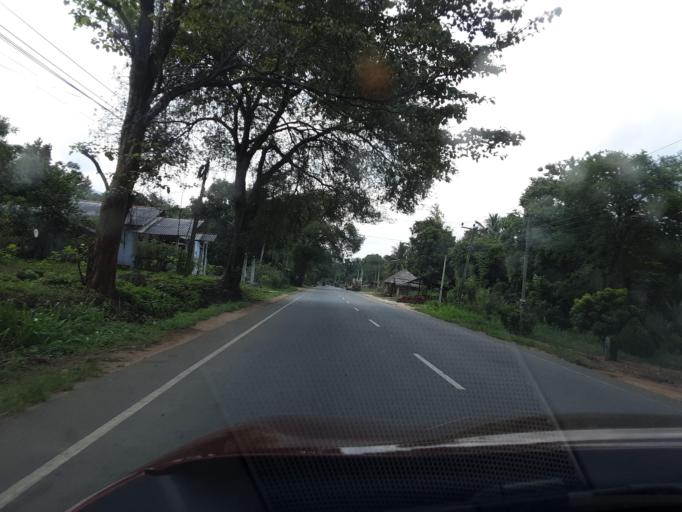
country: LK
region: Uva
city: Haputale
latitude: 6.6983
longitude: 81.1105
